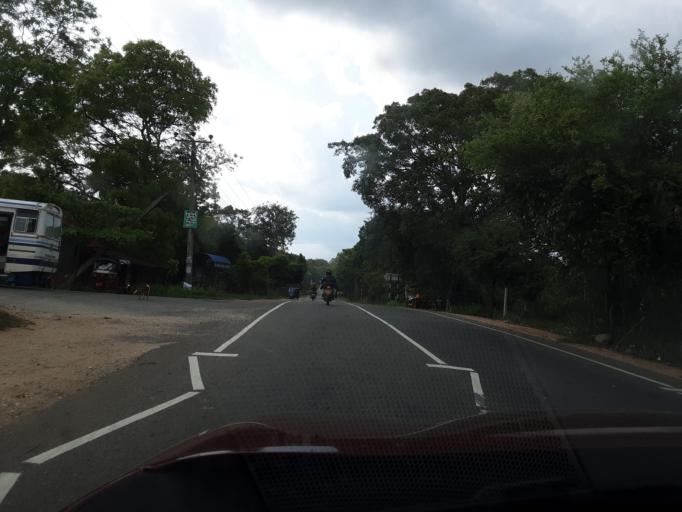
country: LK
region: Uva
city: Haputale
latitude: 6.5184
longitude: 81.1271
